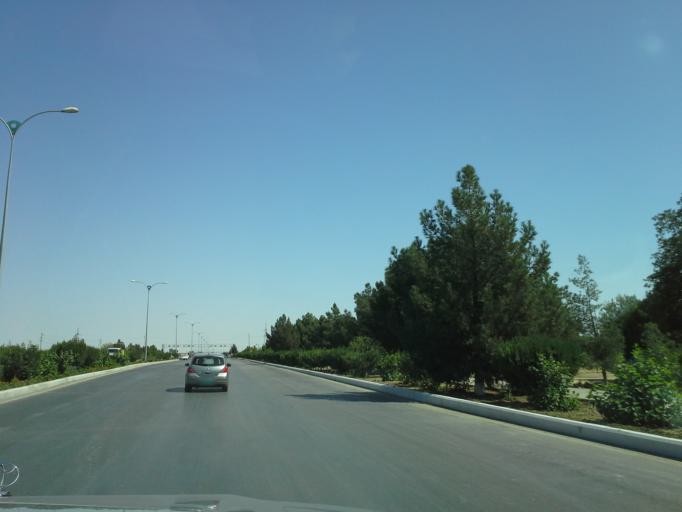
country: TM
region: Ahal
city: Annau
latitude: 37.9175
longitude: 58.4628
